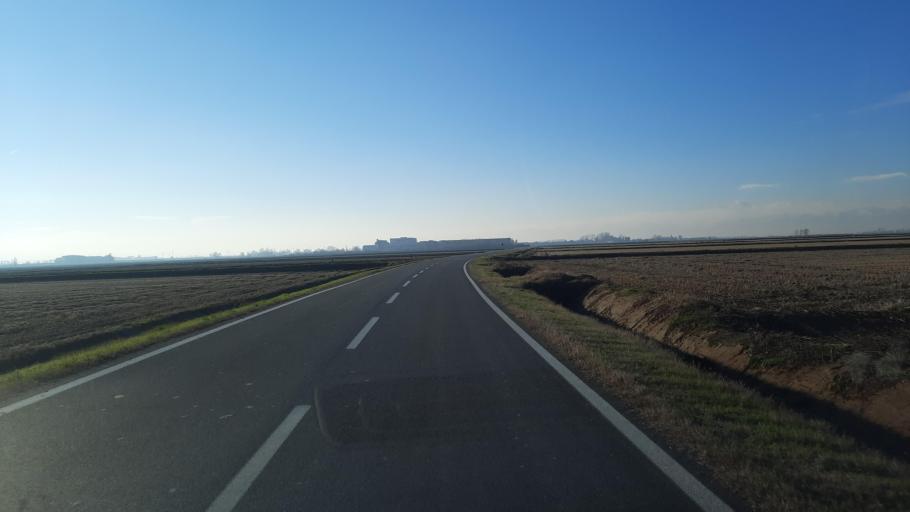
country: IT
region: Piedmont
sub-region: Provincia di Vercelli
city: Pertengo
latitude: 45.2357
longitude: 8.3978
